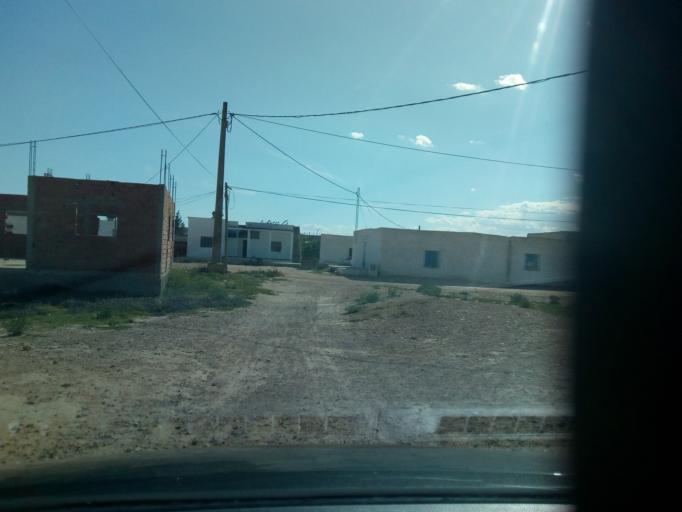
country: TN
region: Safaqis
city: Sfax
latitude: 34.7305
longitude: 10.6028
